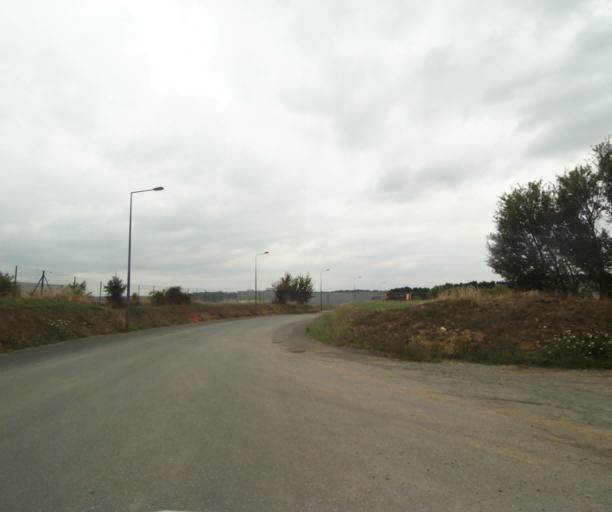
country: FR
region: Pays de la Loire
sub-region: Departement de la Sarthe
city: Solesmes
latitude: 47.8330
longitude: -0.2959
